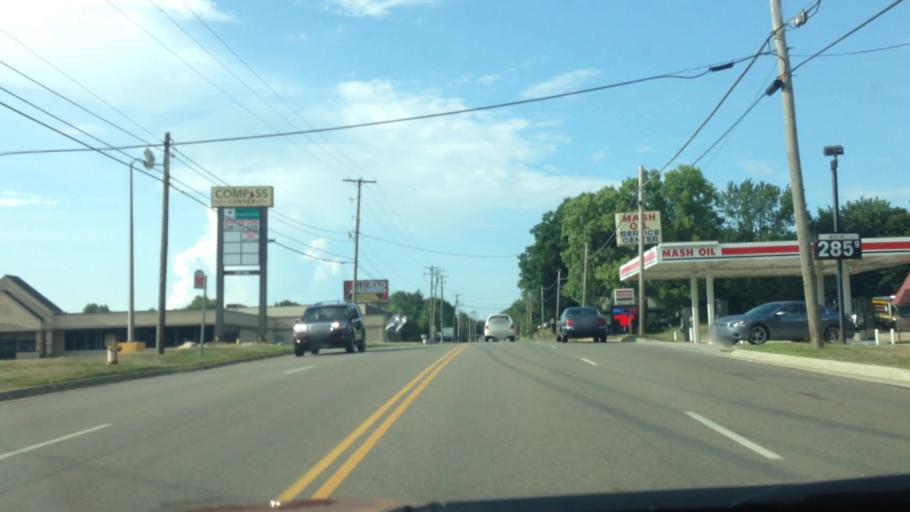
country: US
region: Ohio
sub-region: Summit County
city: Portage Lakes
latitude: 41.0092
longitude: -81.4919
